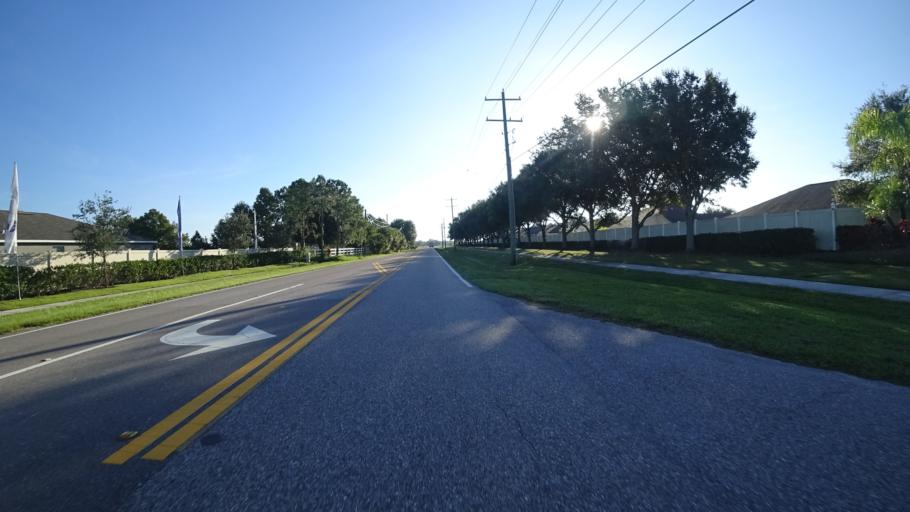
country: US
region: Florida
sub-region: Manatee County
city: Ellenton
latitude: 27.5577
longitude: -82.5305
